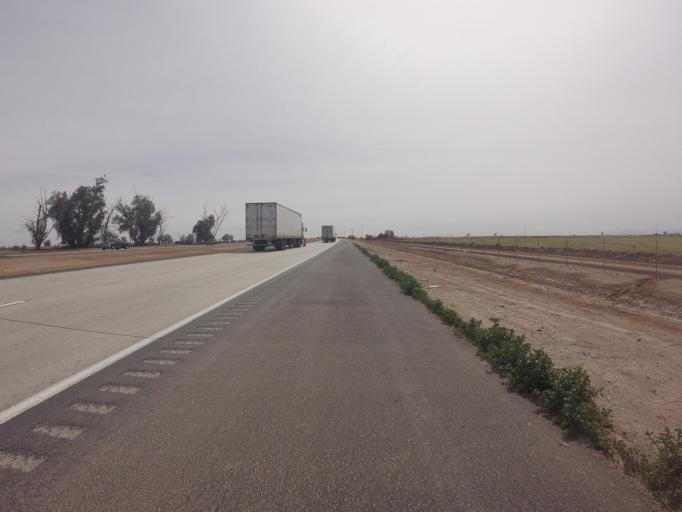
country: US
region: California
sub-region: Imperial County
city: Westmorland
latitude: 33.0107
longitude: -115.5977
